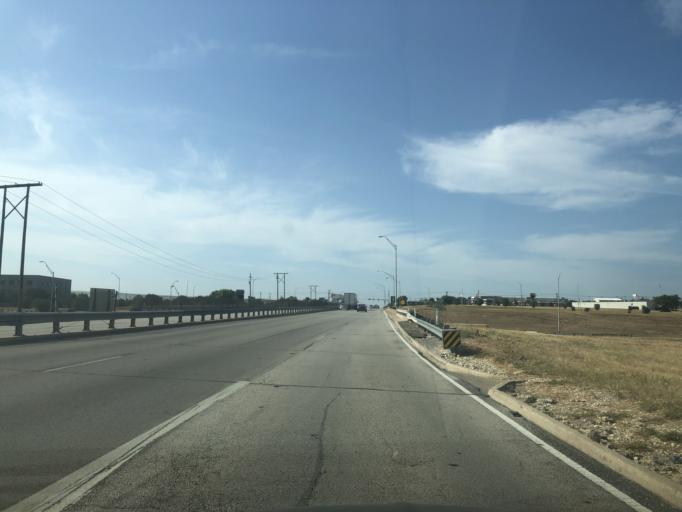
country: US
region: Texas
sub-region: Tarrant County
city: White Settlement
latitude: 32.7376
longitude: -97.4408
